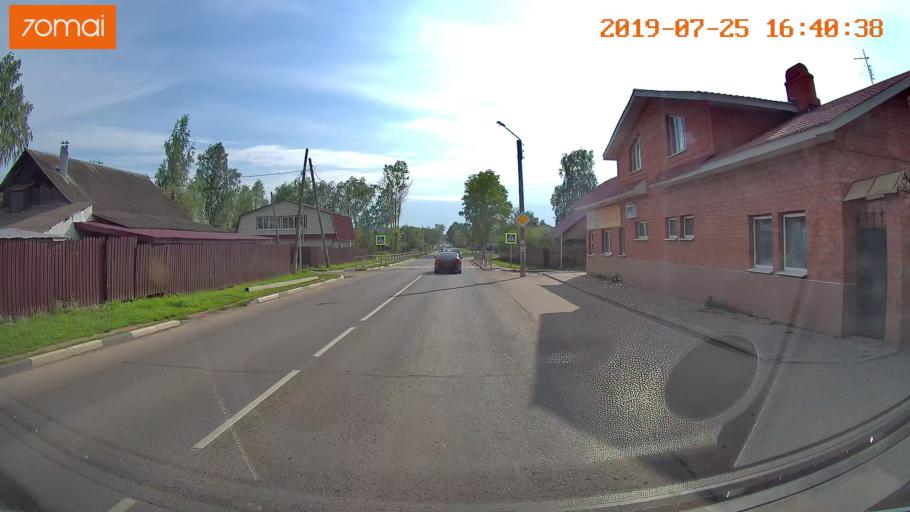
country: RU
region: Ivanovo
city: Privolzhsk
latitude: 57.3844
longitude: 41.3050
